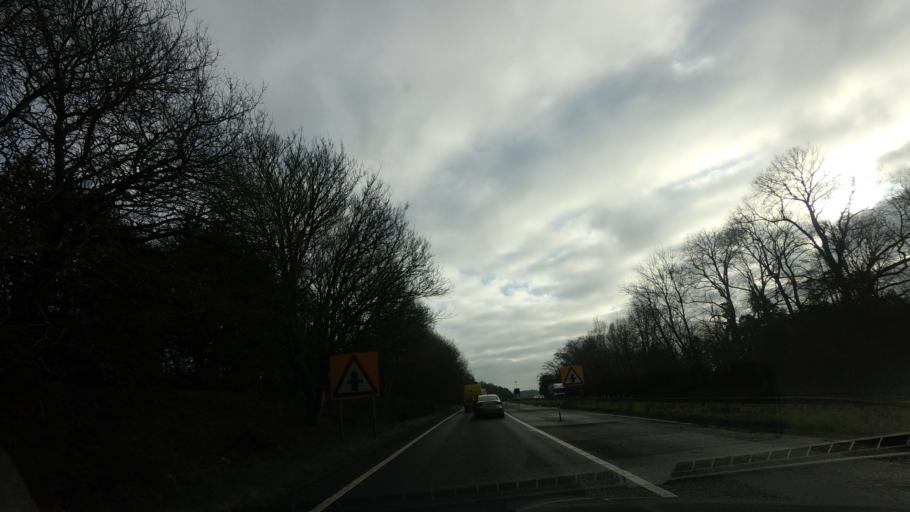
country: GB
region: England
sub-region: Kent
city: Hawkhurst
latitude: 51.0662
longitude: 0.4382
